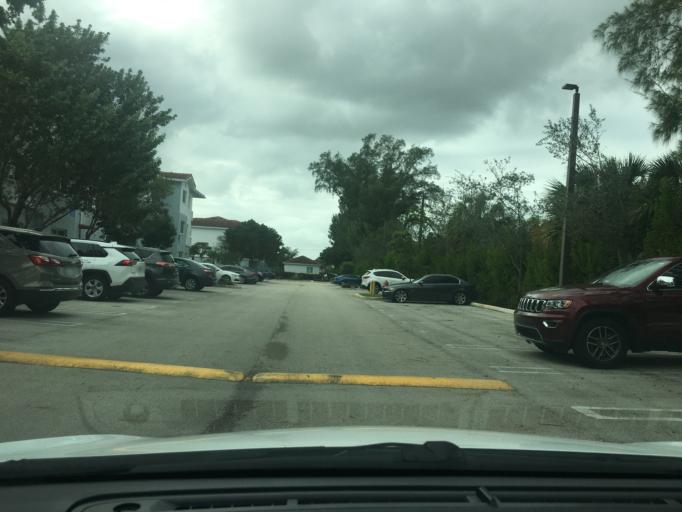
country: US
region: Florida
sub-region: Miami-Dade County
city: Biscayne Park
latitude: 25.8873
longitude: -80.1679
